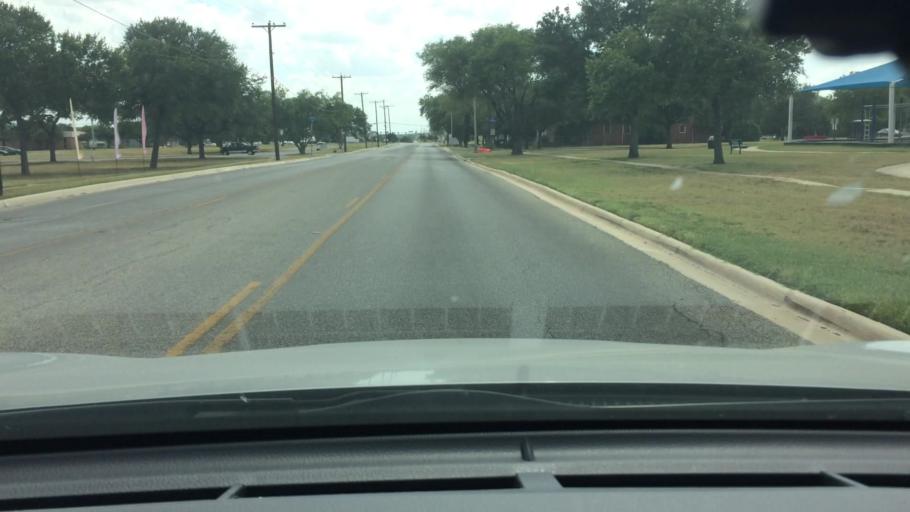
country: US
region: Texas
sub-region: Bexar County
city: San Antonio
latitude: 29.3482
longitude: -98.4405
